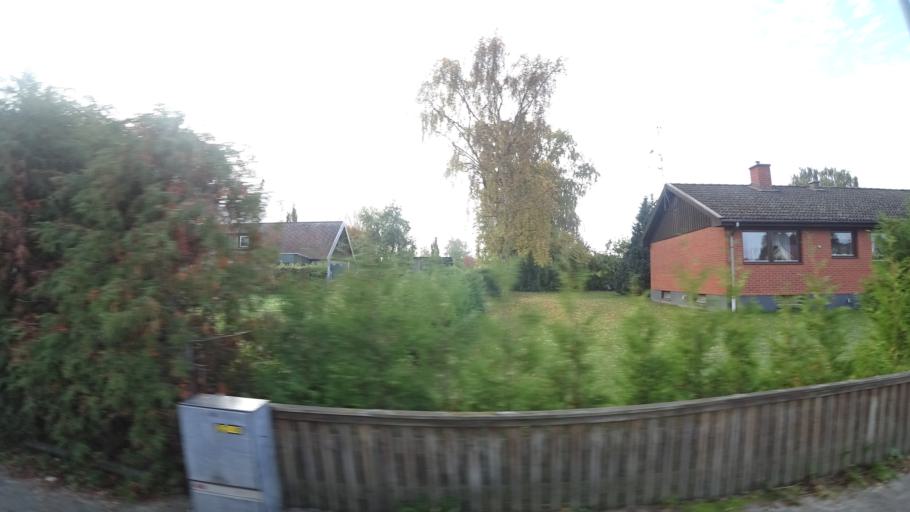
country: SE
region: Skane
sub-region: Staffanstorps Kommun
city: Staffanstorp
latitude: 55.6411
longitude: 13.2022
